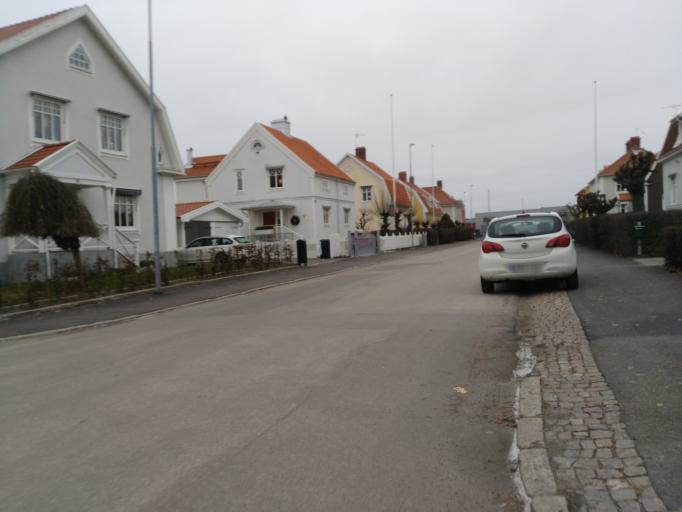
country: SE
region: Vaestra Goetaland
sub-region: Lidkopings Kommun
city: Lidkoping
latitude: 58.5059
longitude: 13.1531
